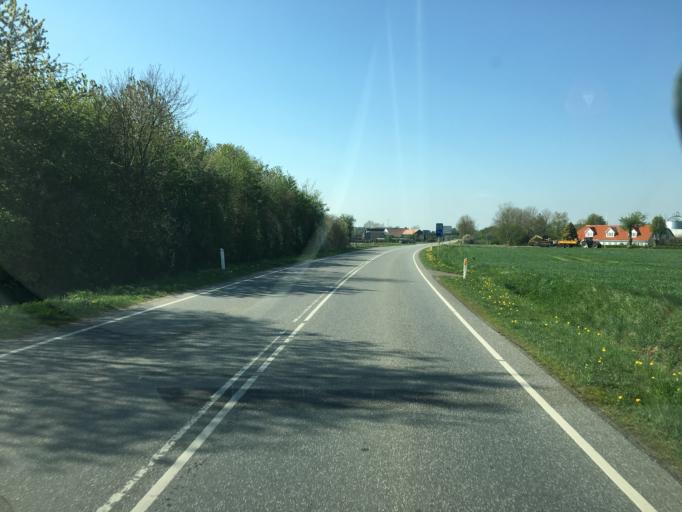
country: DK
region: South Denmark
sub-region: Haderslev Kommune
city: Vojens
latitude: 55.3200
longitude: 9.3145
